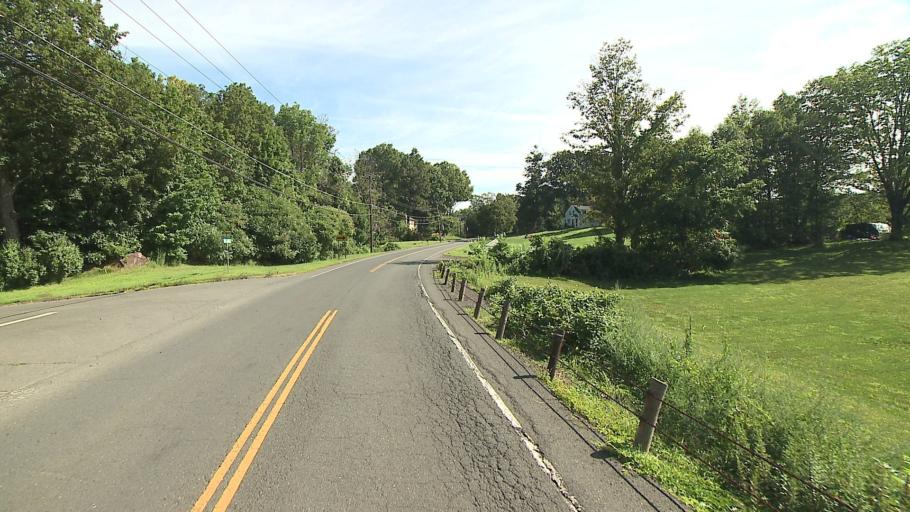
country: US
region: Connecticut
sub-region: Hartford County
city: Tariffville
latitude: 41.9284
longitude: -72.7339
